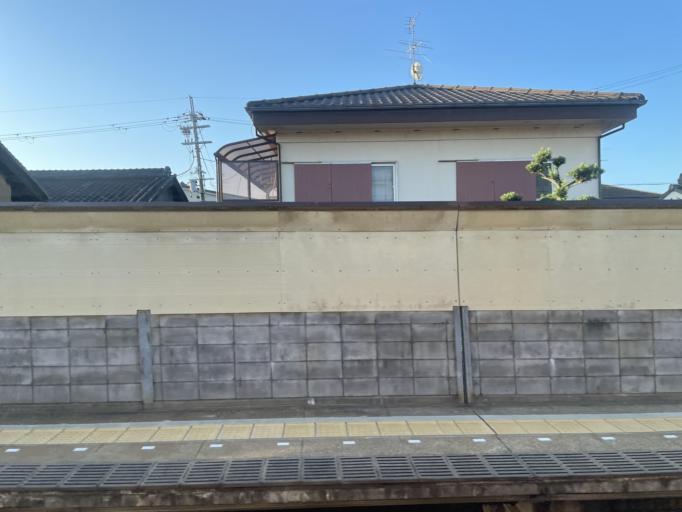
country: JP
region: Nara
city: Kashihara-shi
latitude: 34.5125
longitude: 135.8156
